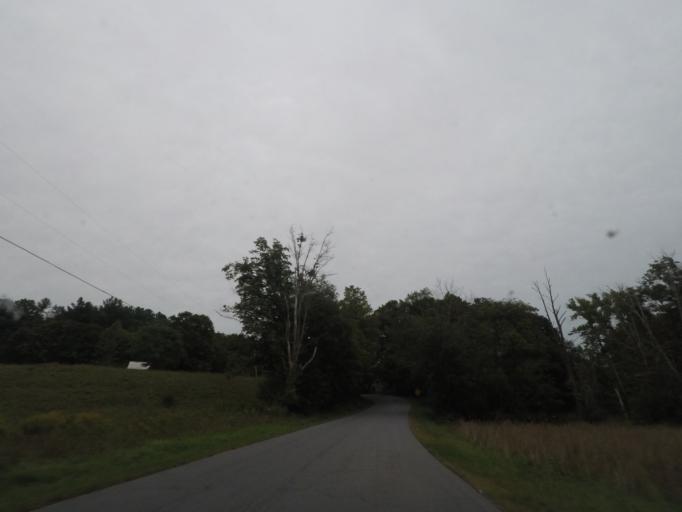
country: US
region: New York
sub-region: Rensselaer County
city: West Sand Lake
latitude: 42.5858
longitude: -73.6004
